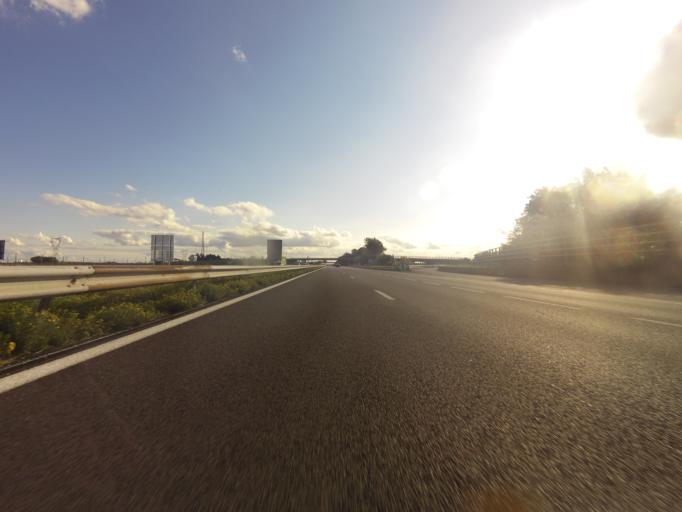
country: FR
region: Picardie
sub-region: Departement de la Somme
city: Chaulnes
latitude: 49.8817
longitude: 2.8374
